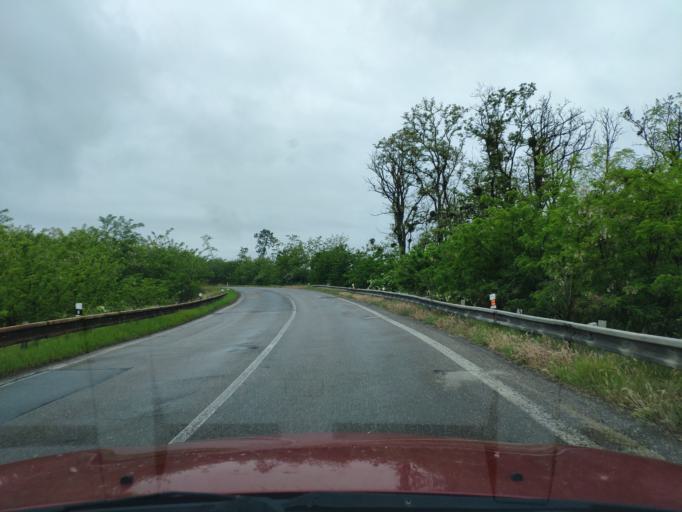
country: HU
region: Borsod-Abauj-Zemplen
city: Ricse
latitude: 48.4410
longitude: 21.9440
